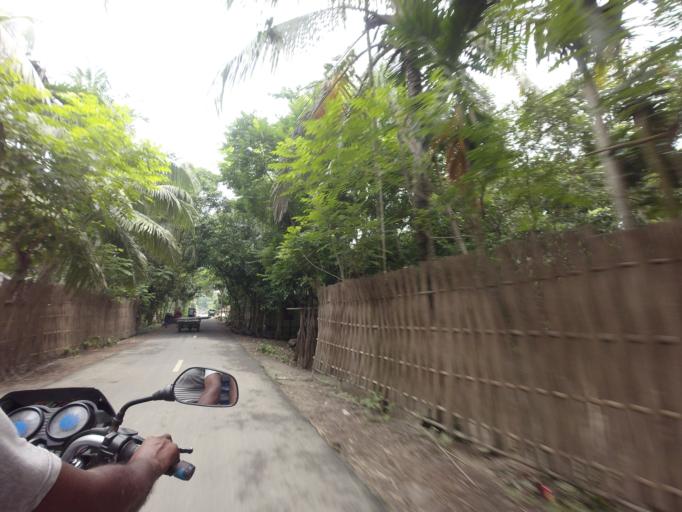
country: BD
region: Khulna
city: Kalia
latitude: 23.1024
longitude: 89.6480
